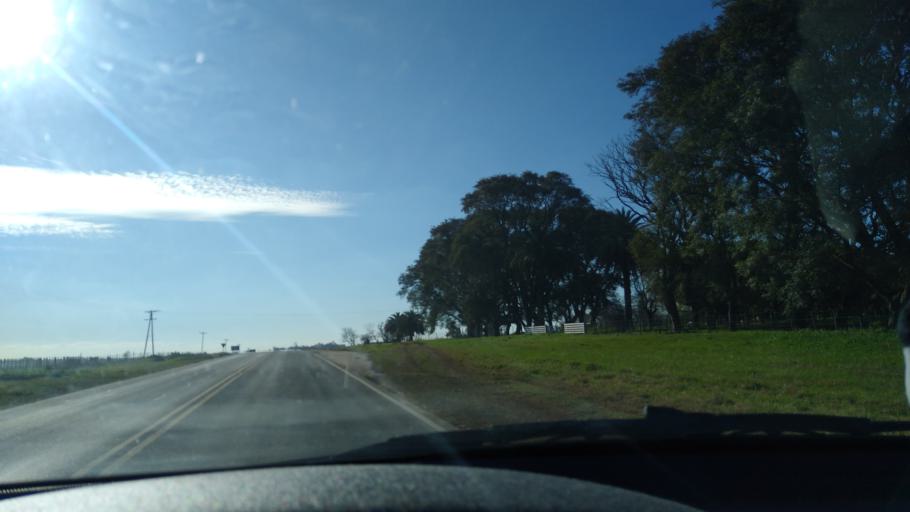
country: AR
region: Entre Rios
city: Aranguren
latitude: -32.3896
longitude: -60.3323
